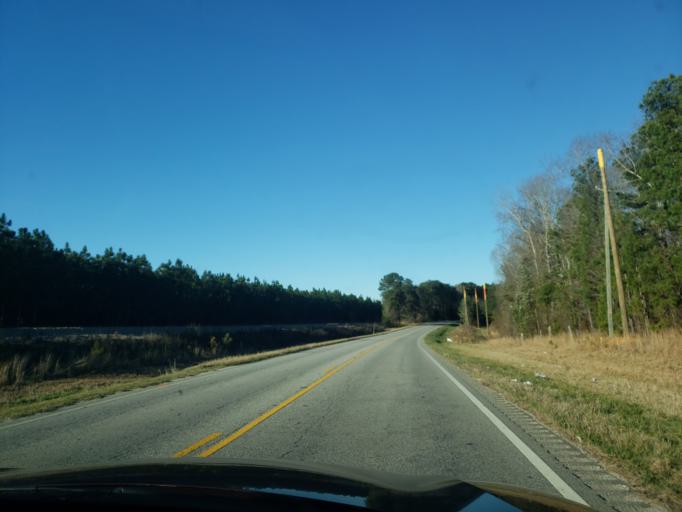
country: US
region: Alabama
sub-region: Lee County
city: Auburn
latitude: 32.5956
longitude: -85.6178
